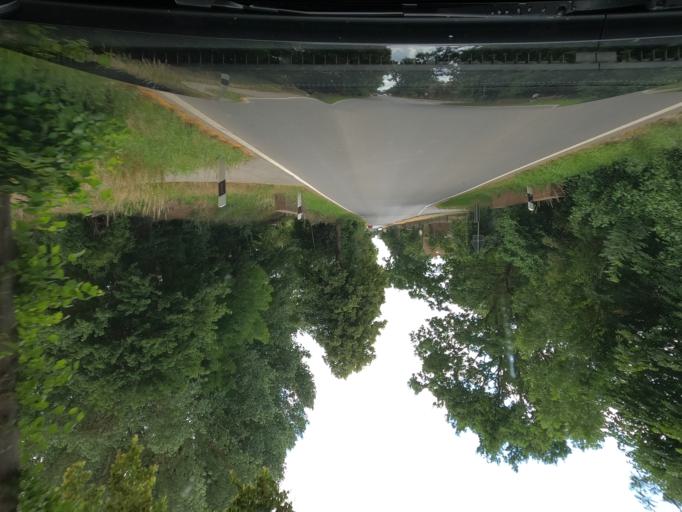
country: DE
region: Lower Saxony
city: Algermissen
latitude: 52.2743
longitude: 10.0134
